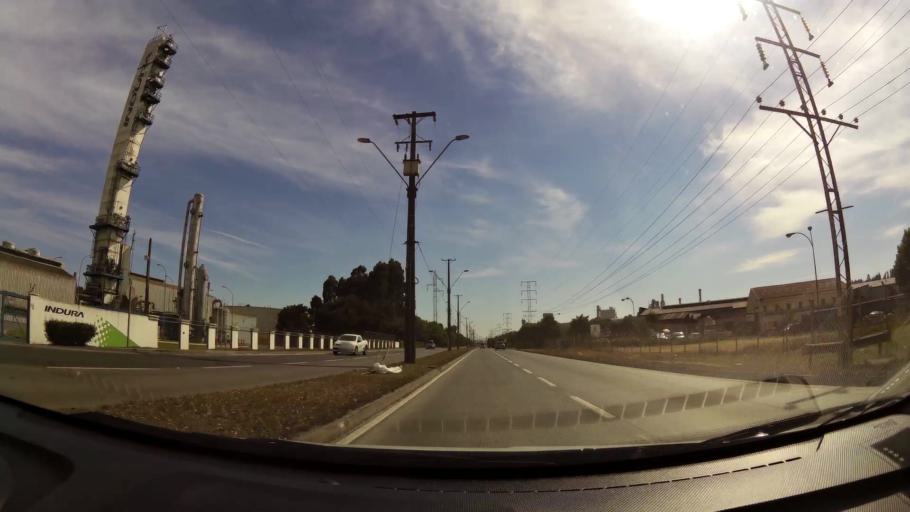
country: CL
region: Biobio
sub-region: Provincia de Concepcion
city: Talcahuano
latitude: -36.7471
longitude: -73.1231
